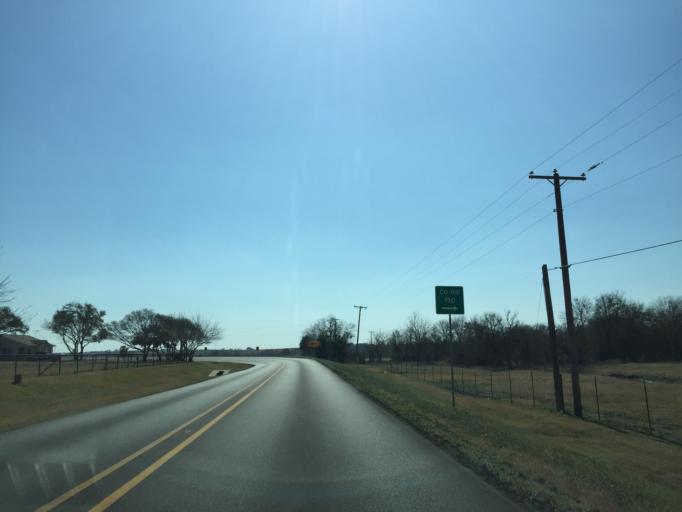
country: US
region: Texas
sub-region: Williamson County
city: Serenada
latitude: 30.7333
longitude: -97.5953
